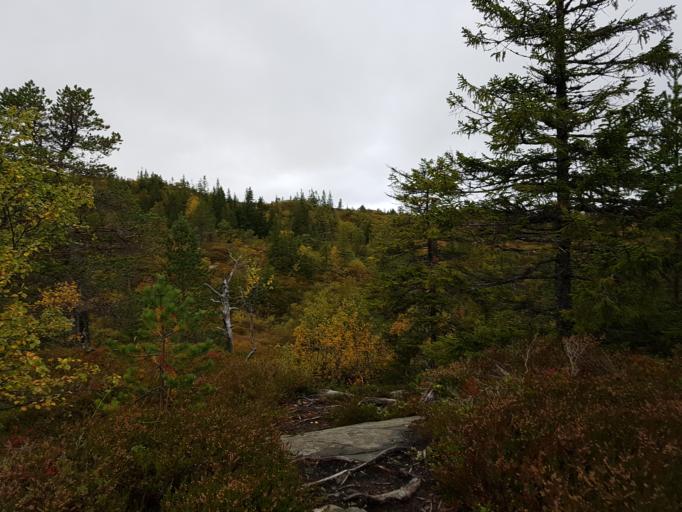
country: NO
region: Sor-Trondelag
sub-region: Melhus
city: Melhus
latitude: 63.4170
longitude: 10.2178
